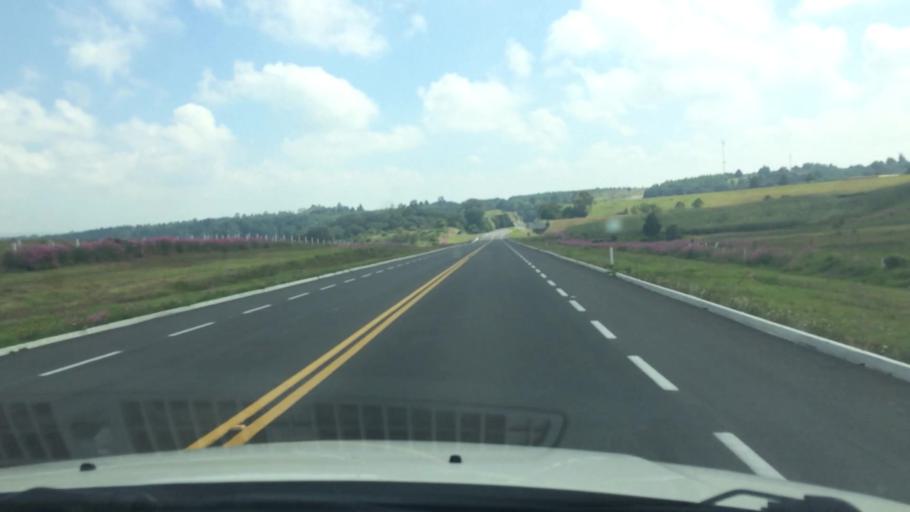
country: MX
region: Mexico
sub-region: Villa Victoria
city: Colonia Doctor Gustavo Baz
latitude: 19.3743
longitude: -99.9116
